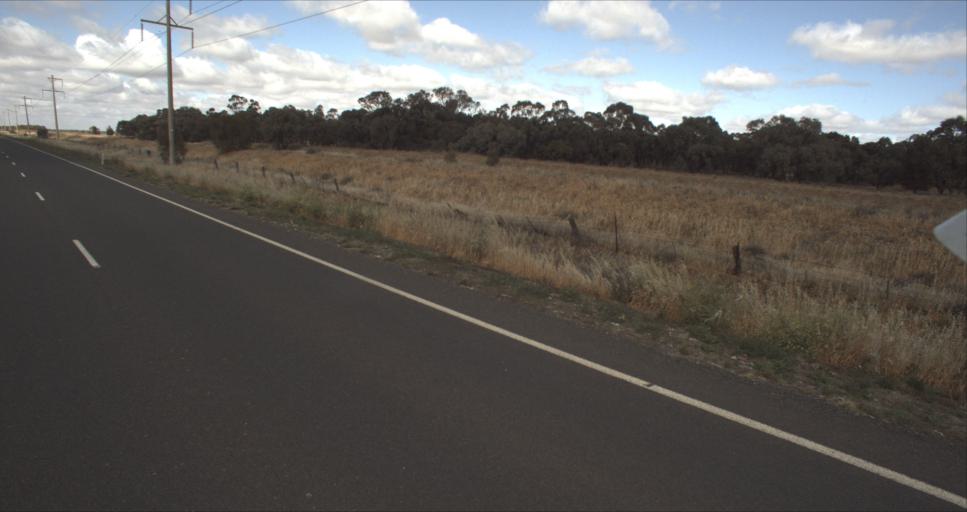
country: AU
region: New South Wales
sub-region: Murrumbidgee Shire
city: Darlington Point
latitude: -34.5423
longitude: 146.1719
